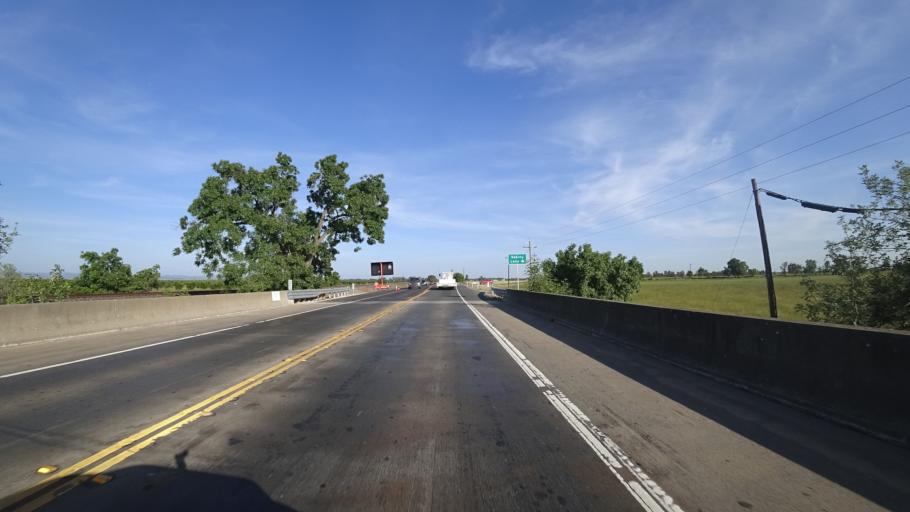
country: US
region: California
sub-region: Yuba County
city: Wheatland
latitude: 39.0355
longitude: -121.4641
